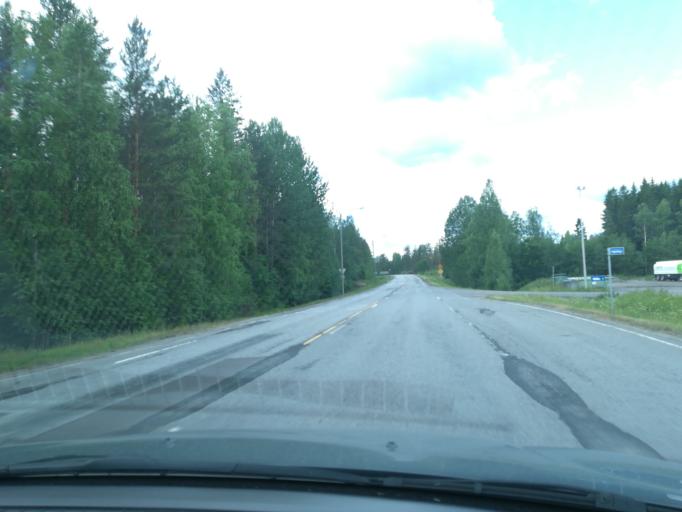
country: FI
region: Southern Savonia
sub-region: Mikkeli
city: Ristiina
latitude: 61.4525
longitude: 27.2632
